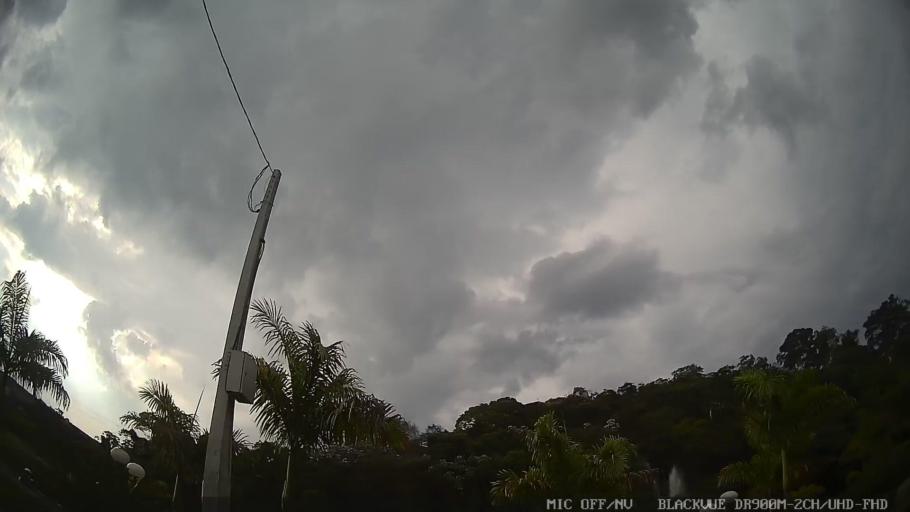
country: BR
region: Sao Paulo
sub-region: Itatiba
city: Itatiba
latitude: -23.0276
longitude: -46.8476
